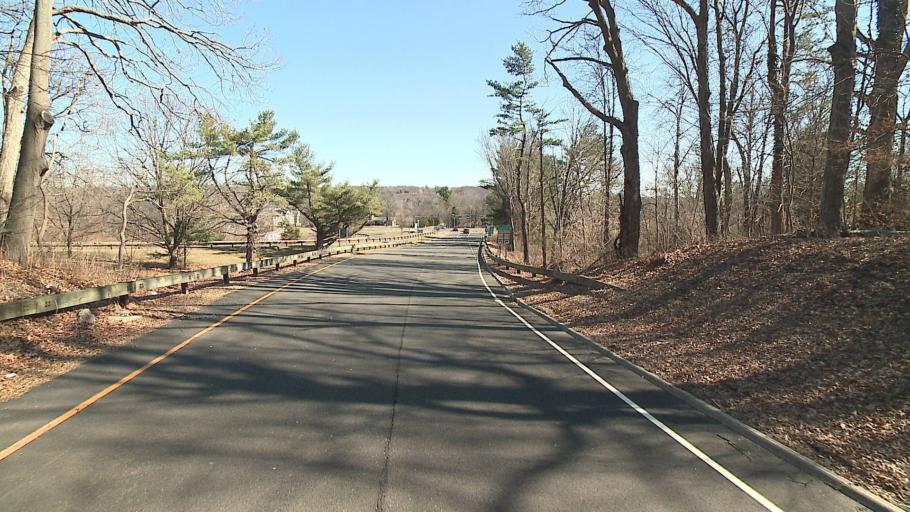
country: US
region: Connecticut
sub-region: New Haven County
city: City of Milford (balance)
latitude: 41.2434
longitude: -73.1061
